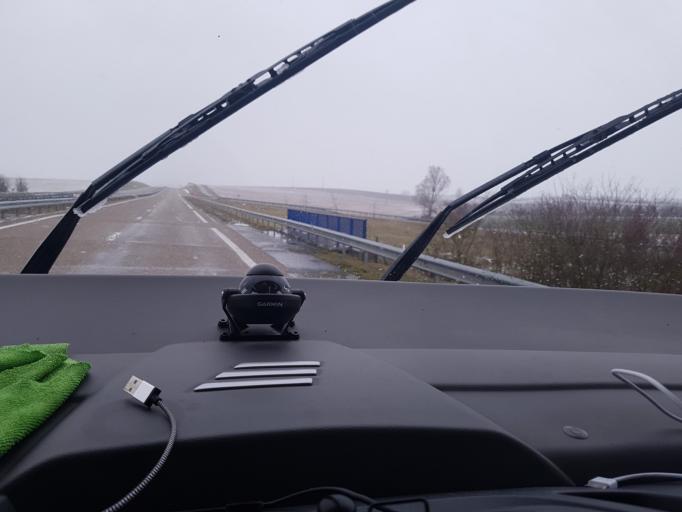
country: FR
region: Lorraine
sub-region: Departement de la Moselle
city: Dieuze
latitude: 48.7406
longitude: 6.6641
